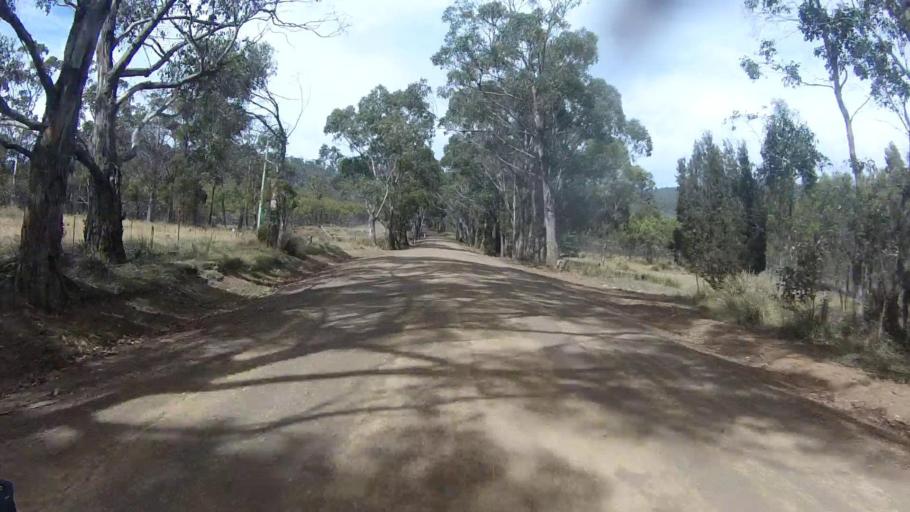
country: AU
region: Tasmania
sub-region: Sorell
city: Sorell
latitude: -42.6617
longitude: 147.8933
